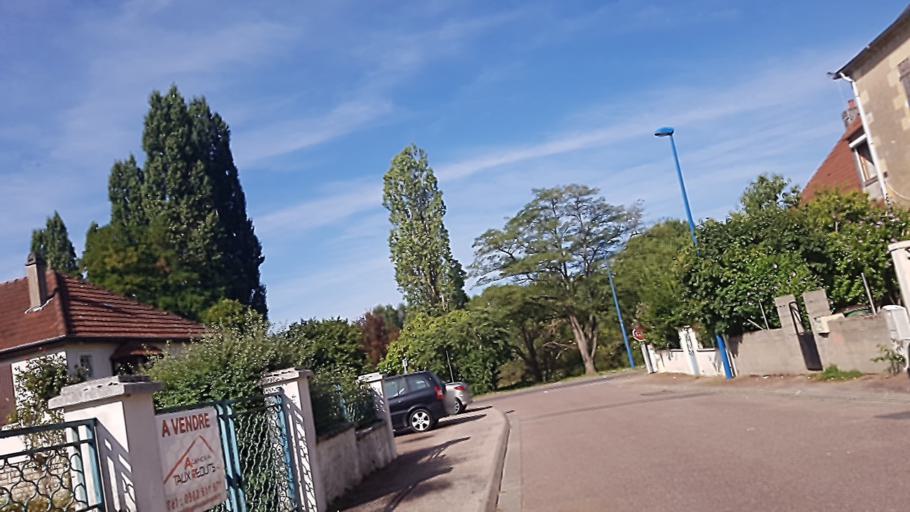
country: FR
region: Bourgogne
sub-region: Departement de la Nievre
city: Imphy
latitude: 46.9264
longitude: 3.2595
